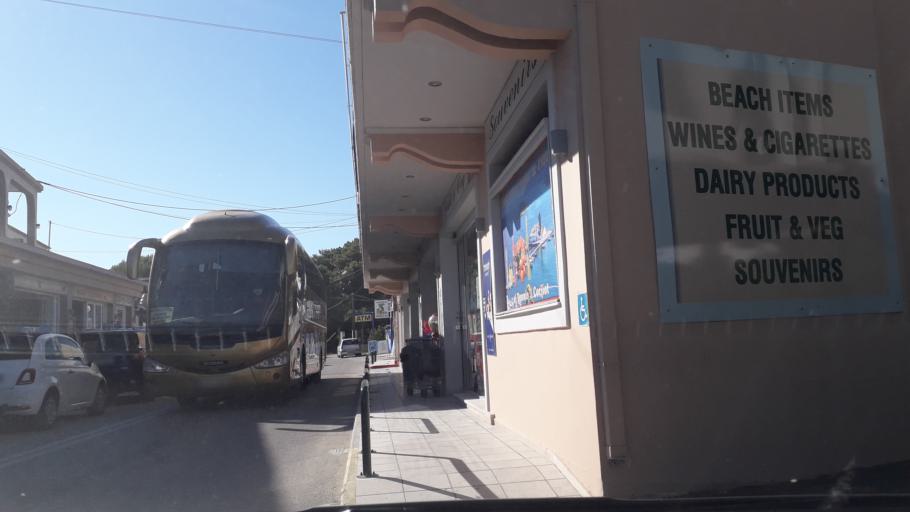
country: GR
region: Ionian Islands
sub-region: Nomos Kerkyras
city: Perivoli
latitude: 39.4273
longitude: 19.9433
